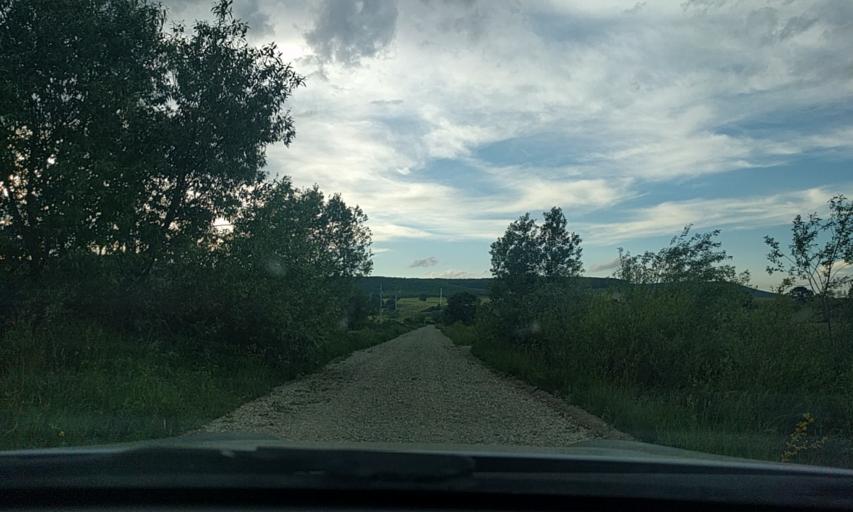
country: RO
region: Covasna
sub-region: Comuna Ilieni
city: Ilieni
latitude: 45.7642
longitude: 25.7195
